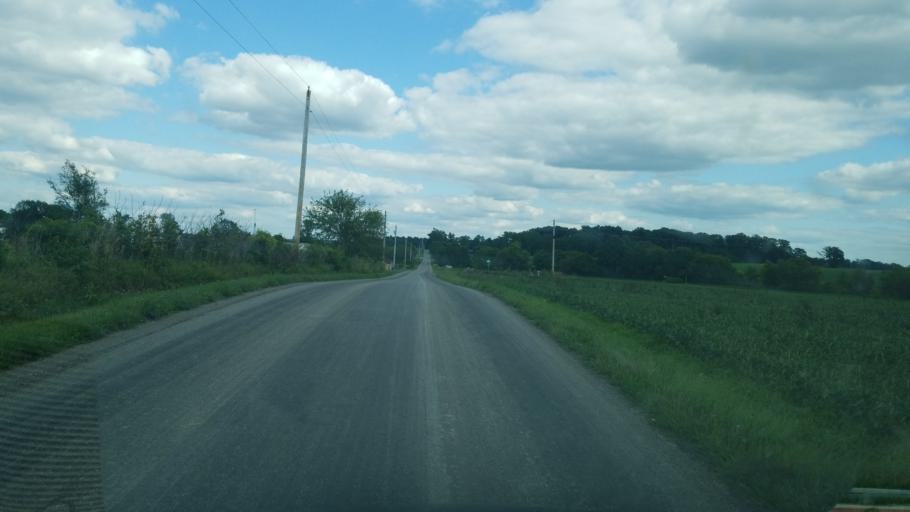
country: US
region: Ohio
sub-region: Logan County
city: De Graff
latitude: 40.3764
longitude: -83.8890
